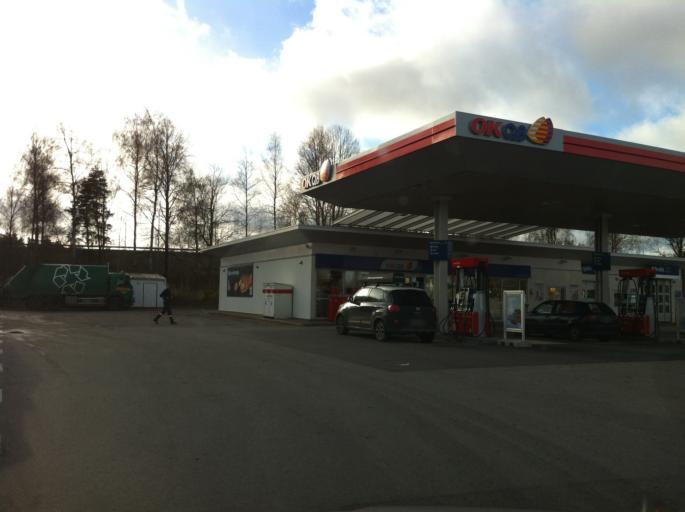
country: SE
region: Kronoberg
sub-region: Vaxjo Kommun
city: Vaexjoe
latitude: 56.8556
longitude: 14.7304
